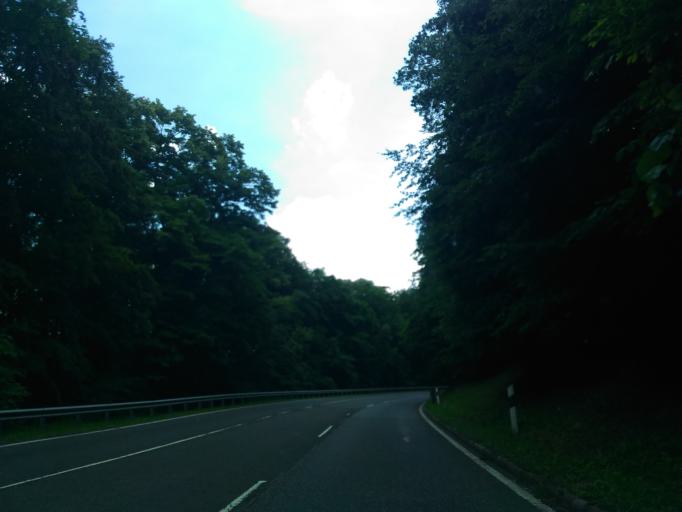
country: HU
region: Baranya
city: Komlo
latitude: 46.1536
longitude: 18.2433
